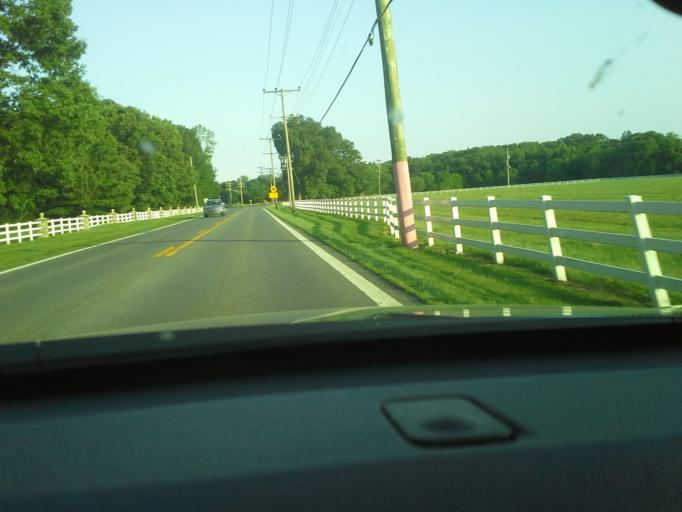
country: US
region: Maryland
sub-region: Anne Arundel County
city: Deale
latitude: 38.8192
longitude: -76.5575
